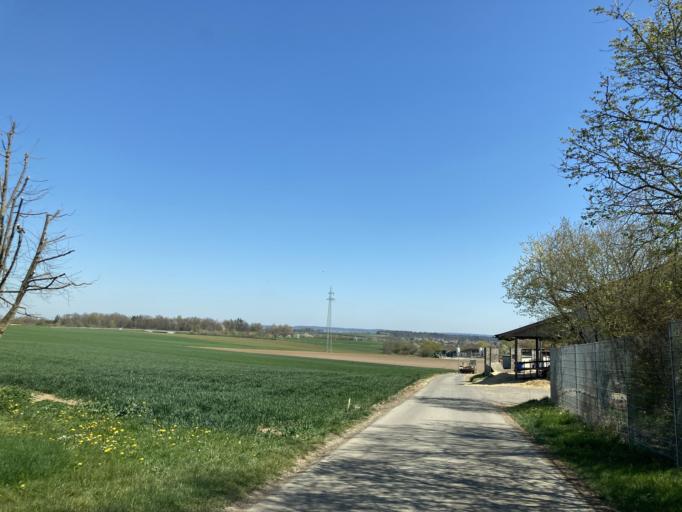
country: DE
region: Baden-Wuerttemberg
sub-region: Regierungsbezirk Stuttgart
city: Bondorf
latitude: 48.4946
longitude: 8.8513
